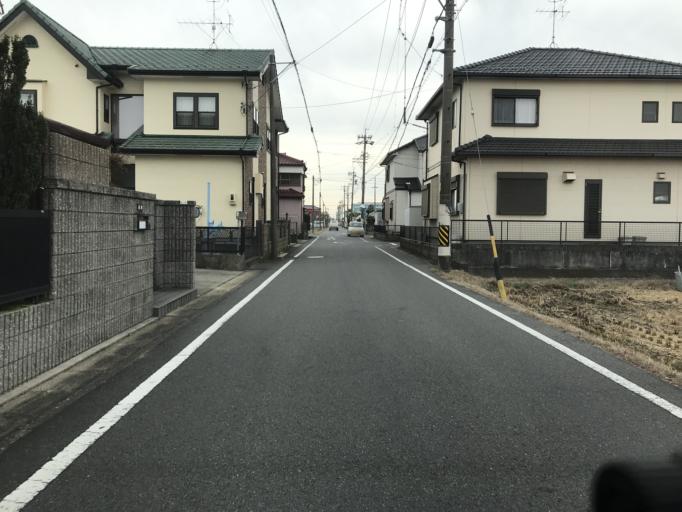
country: JP
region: Aichi
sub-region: Aisai-shi
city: Aisai
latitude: 35.1774
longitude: 136.7782
